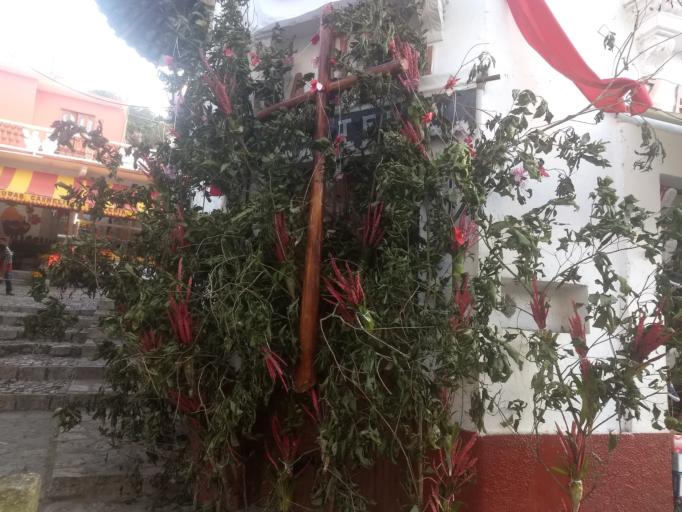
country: MX
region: Puebla
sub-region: Cuetzalan del Progreso
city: Ciudad de Cuetzalan
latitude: 20.0188
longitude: -97.5221
